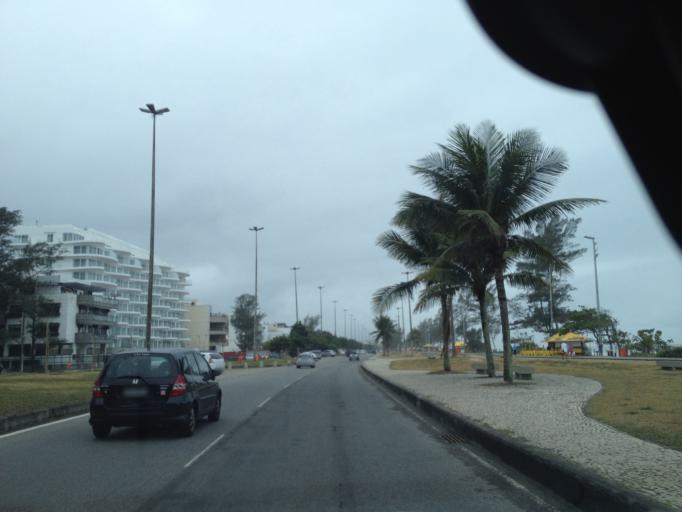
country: BR
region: Rio de Janeiro
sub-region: Nilopolis
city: Nilopolis
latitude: -23.0282
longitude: -43.4662
